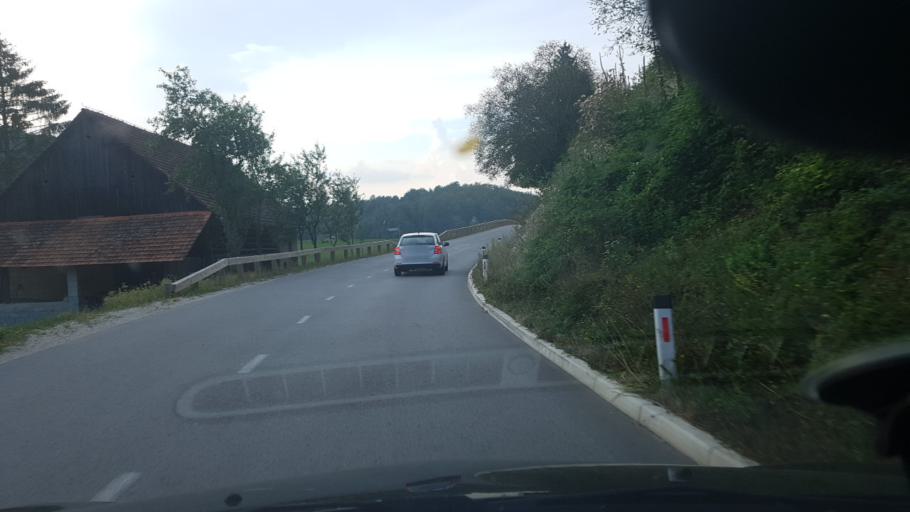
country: SI
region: Kozje
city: Kozje
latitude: 46.0850
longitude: 15.5707
